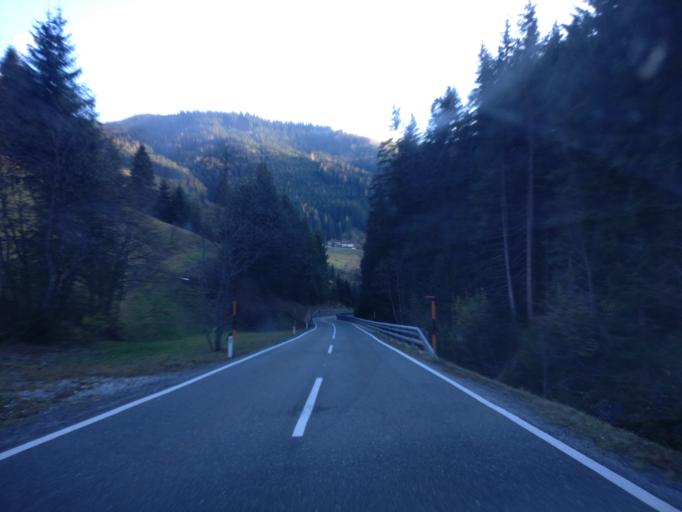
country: AT
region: Salzburg
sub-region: Politischer Bezirk Zell am See
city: Dienten am Hochkonig
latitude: 47.3930
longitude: 13.0152
